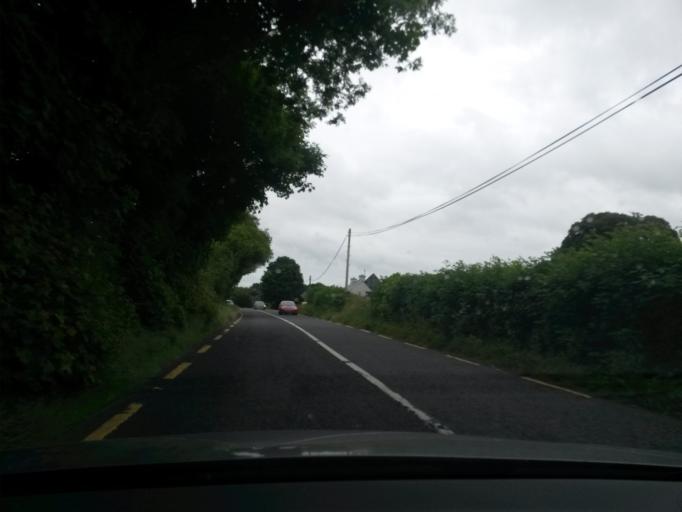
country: IE
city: Ballisodare
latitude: 54.2023
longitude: -8.5710
